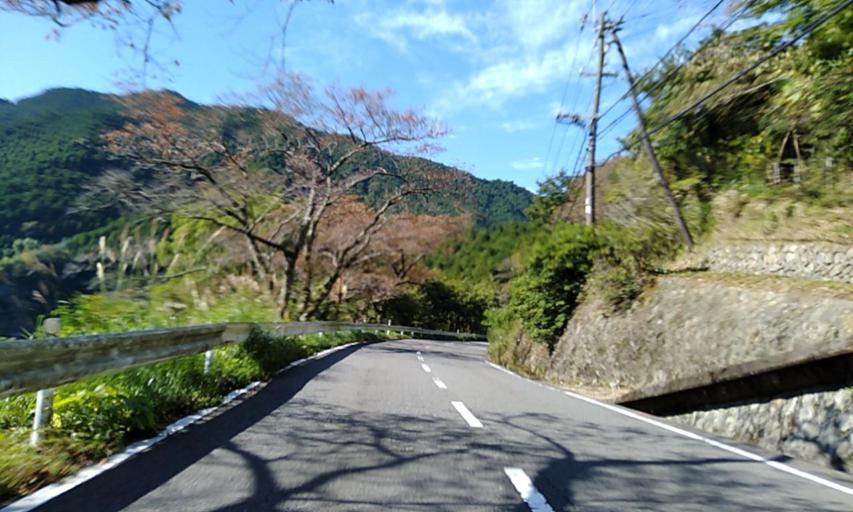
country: JP
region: Wakayama
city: Iwade
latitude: 34.0861
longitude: 135.3601
